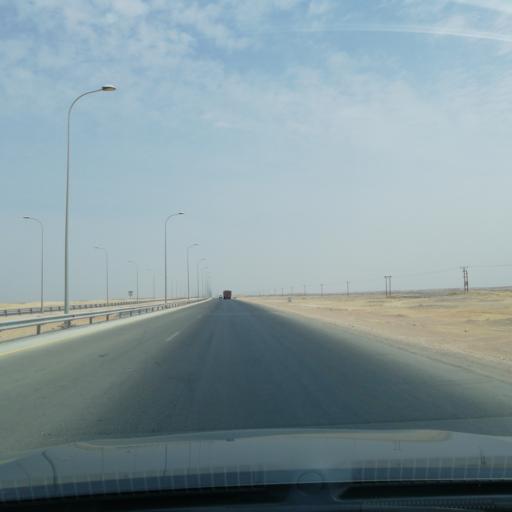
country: OM
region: Zufar
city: Salalah
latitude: 17.6671
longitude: 54.0566
